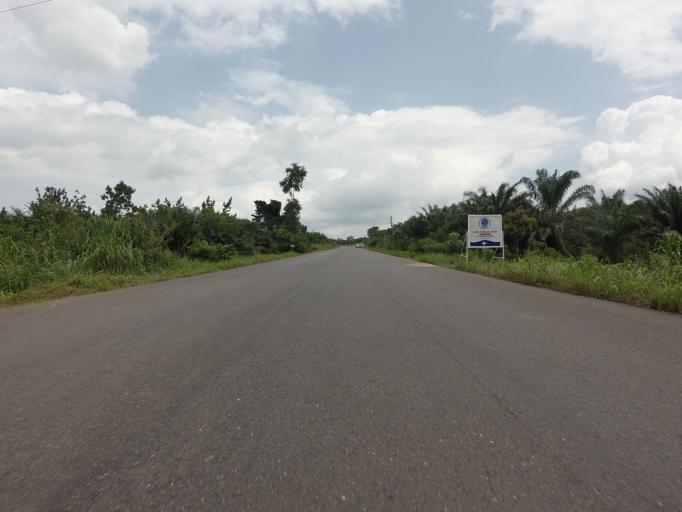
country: GH
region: Volta
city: Ho
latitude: 6.5247
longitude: 0.2227
